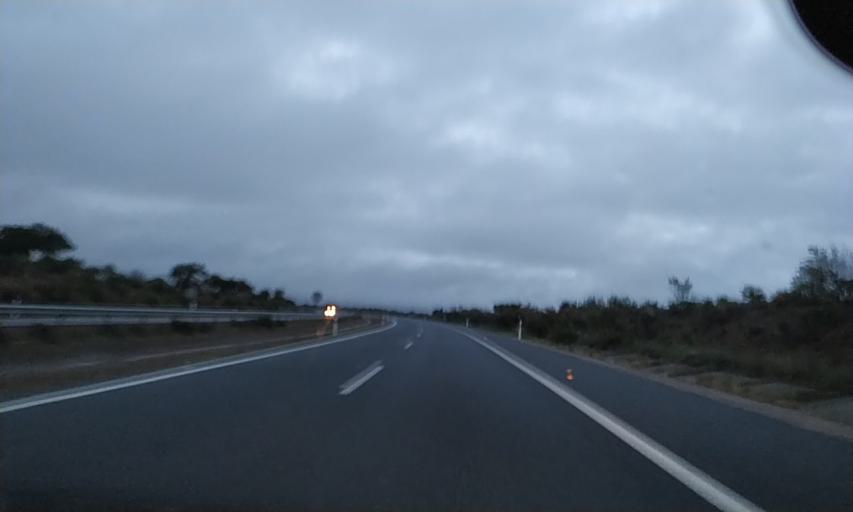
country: ES
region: Extremadura
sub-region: Provincia de Badajoz
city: Aljucen
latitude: 39.0835
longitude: -6.2976
